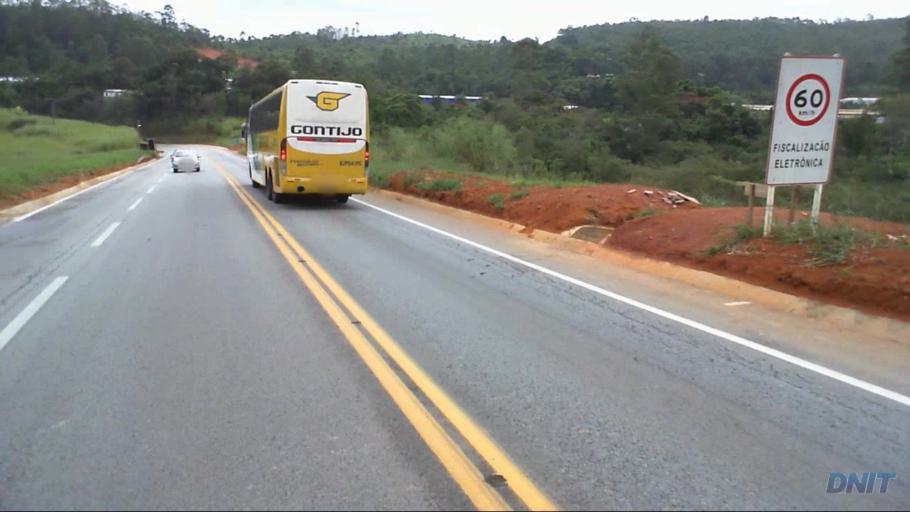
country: BR
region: Minas Gerais
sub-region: Joao Monlevade
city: Joao Monlevade
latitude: -19.8612
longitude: -43.1240
